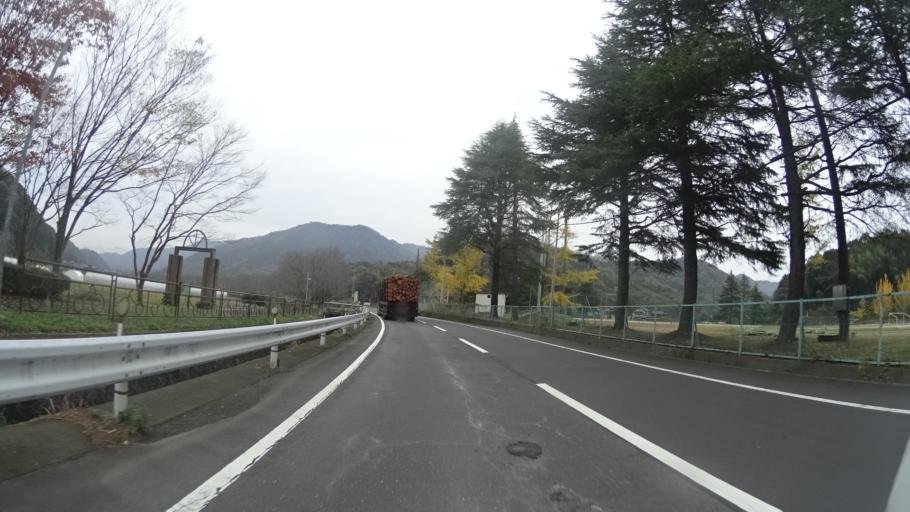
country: JP
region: Kyoto
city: Maizuru
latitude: 35.4963
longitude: 135.4379
